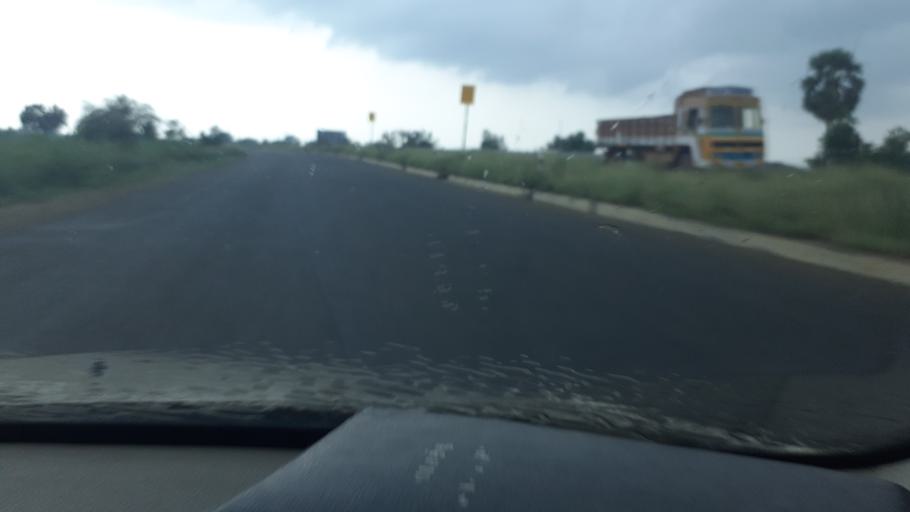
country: IN
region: Tamil Nadu
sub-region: Thoothukkudi
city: Kadambur
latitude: 9.0813
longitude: 77.8015
